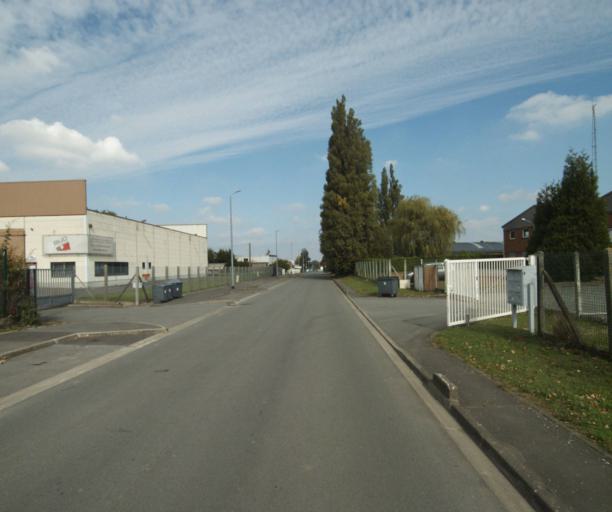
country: FR
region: Nord-Pas-de-Calais
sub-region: Departement du Nord
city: Seclin
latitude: 50.5608
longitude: 3.0402
